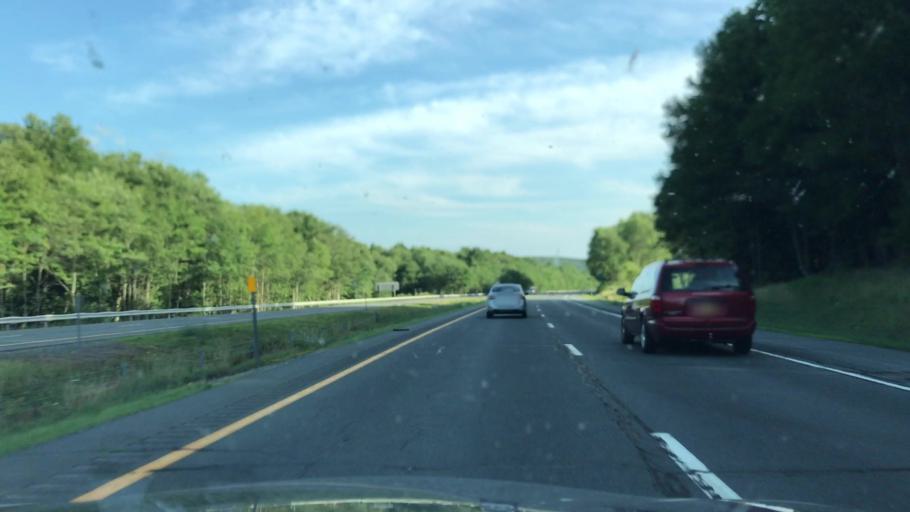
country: US
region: New York
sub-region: Sullivan County
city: Liberty
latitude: 41.7306
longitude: -74.7279
